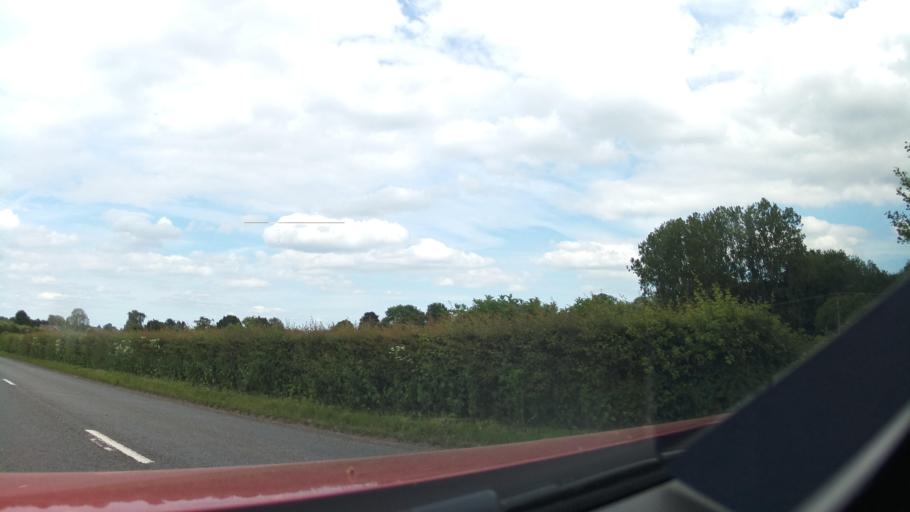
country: GB
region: England
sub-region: Herefordshire
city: Yatton
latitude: 51.9931
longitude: -2.5039
